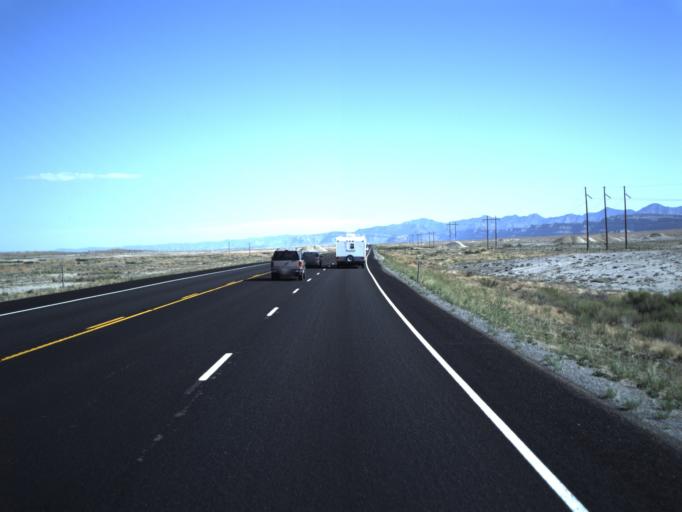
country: US
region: Utah
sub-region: Carbon County
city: East Carbon City
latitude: 39.1564
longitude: -110.3381
